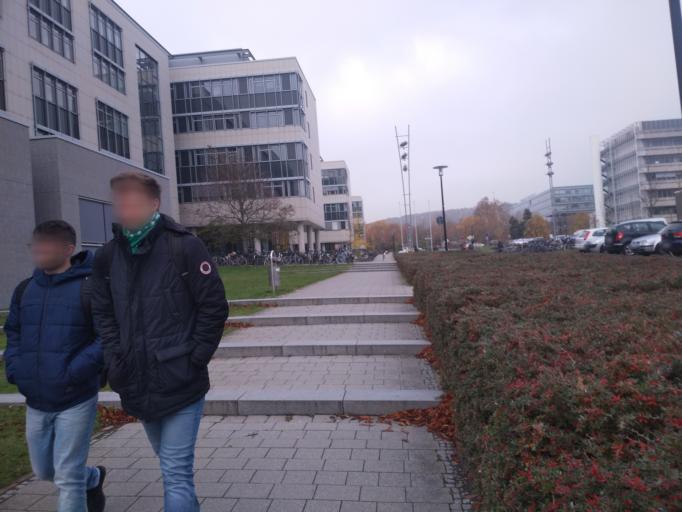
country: DE
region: Lower Saxony
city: Goettingen
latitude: 51.5576
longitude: 9.9469
